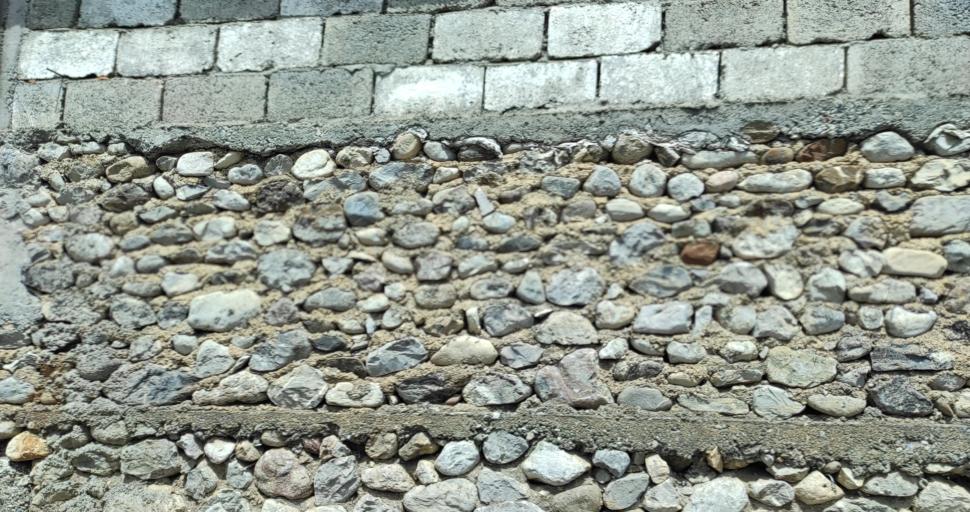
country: AL
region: Shkoder
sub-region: Rrethi i Malesia e Madhe
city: Gruemire
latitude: 42.1200
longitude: 19.5754
